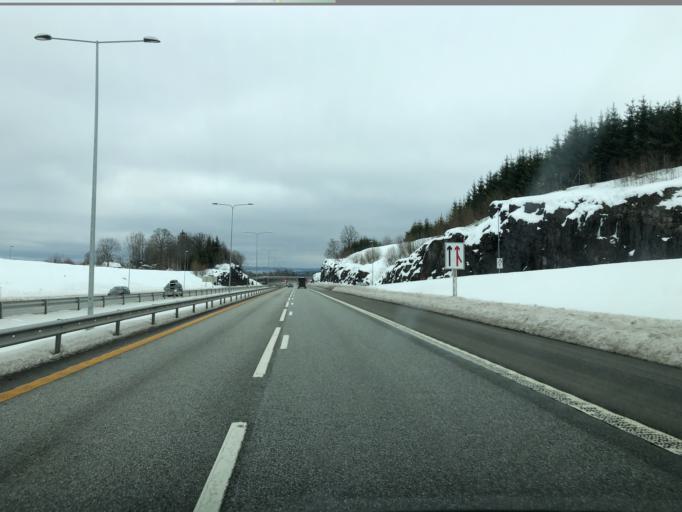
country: NO
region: Vestfold
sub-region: Holmestrand
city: Holmestrand
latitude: 59.4684
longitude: 10.3162
